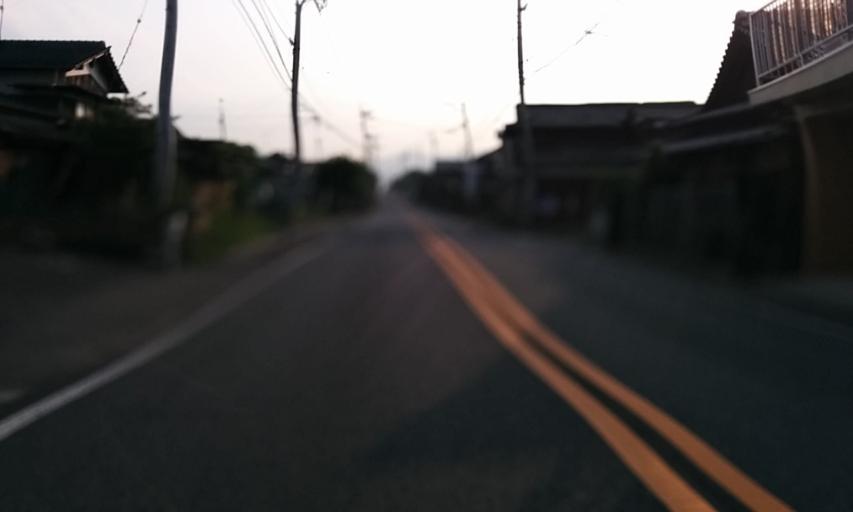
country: JP
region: Ehime
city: Saijo
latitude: 33.8813
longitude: 133.0755
